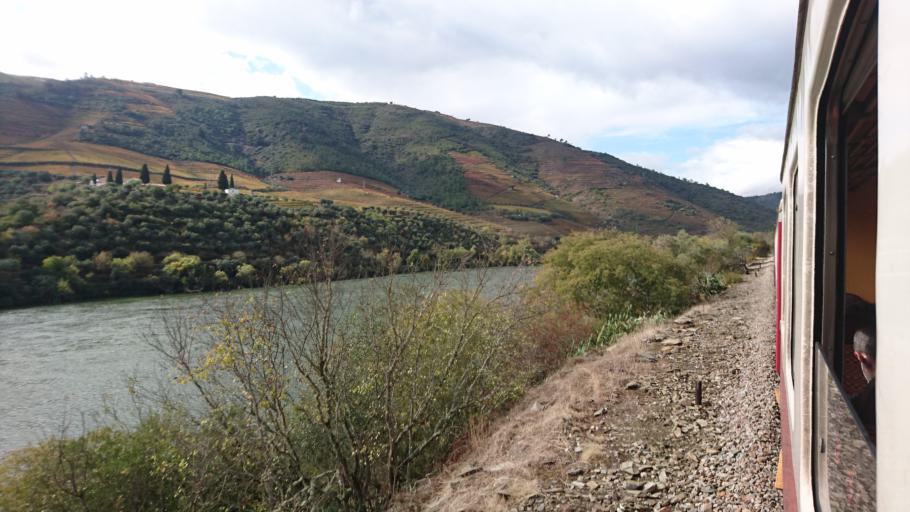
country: PT
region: Viseu
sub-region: Sao Joao da Pesqueira
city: Sao Joao da Pesqueira
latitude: 41.2001
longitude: -7.4746
